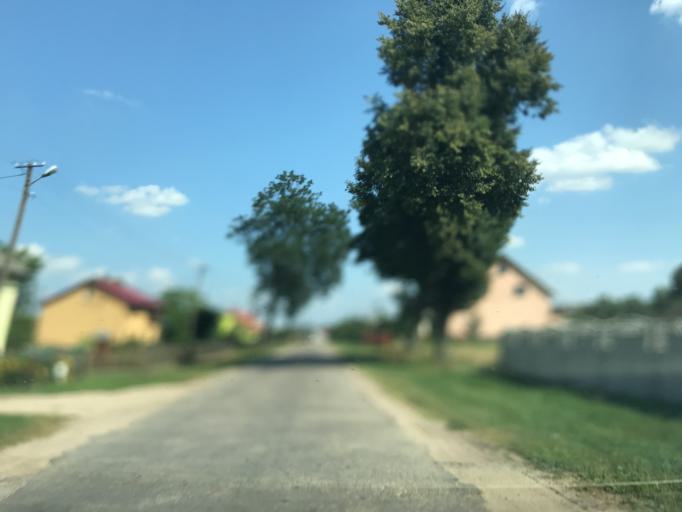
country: PL
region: Masovian Voivodeship
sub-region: Powiat zurominski
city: Lubowidz
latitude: 53.1733
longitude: 19.8914
